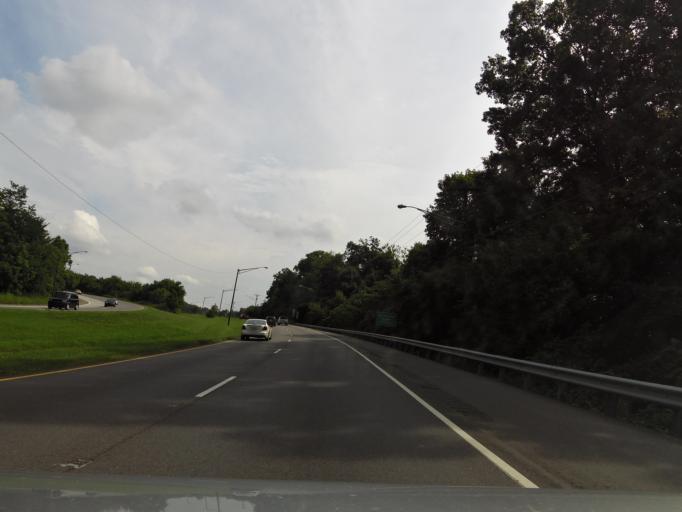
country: US
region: Tennessee
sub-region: Knox County
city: Knoxville
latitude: 35.8900
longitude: -83.9549
